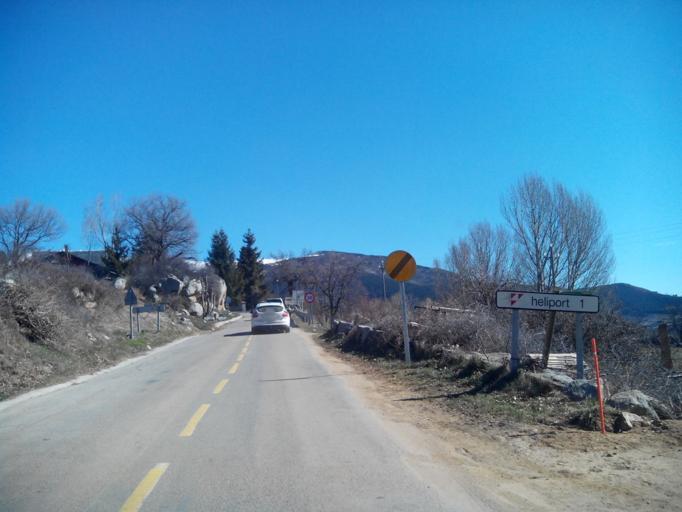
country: ES
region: Catalonia
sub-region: Provincia de Lleida
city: Lles de Cerdanya
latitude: 42.3882
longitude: 1.6870
